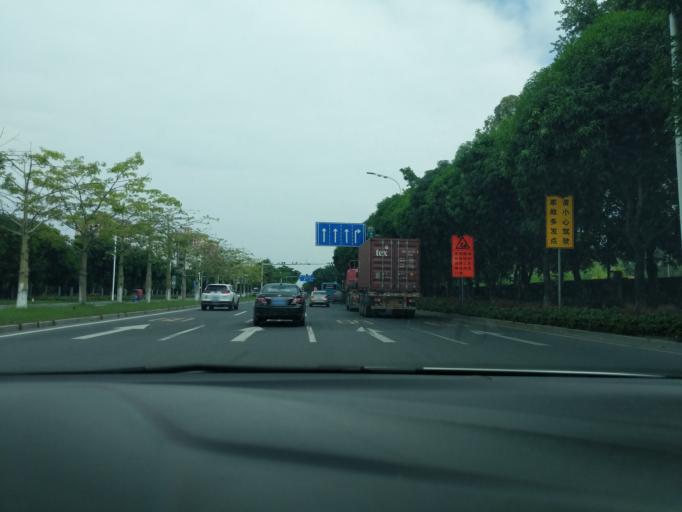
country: CN
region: Guangdong
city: Nansha
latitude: 22.7509
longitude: 113.5798
